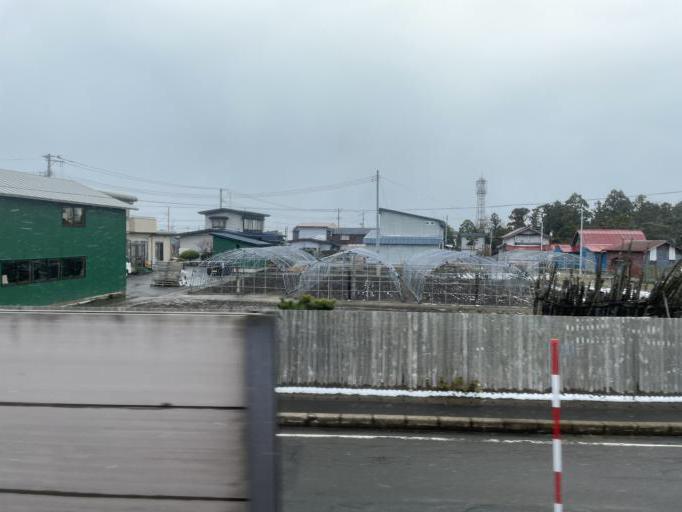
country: JP
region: Aomori
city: Aomori Shi
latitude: 40.9663
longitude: 140.6547
